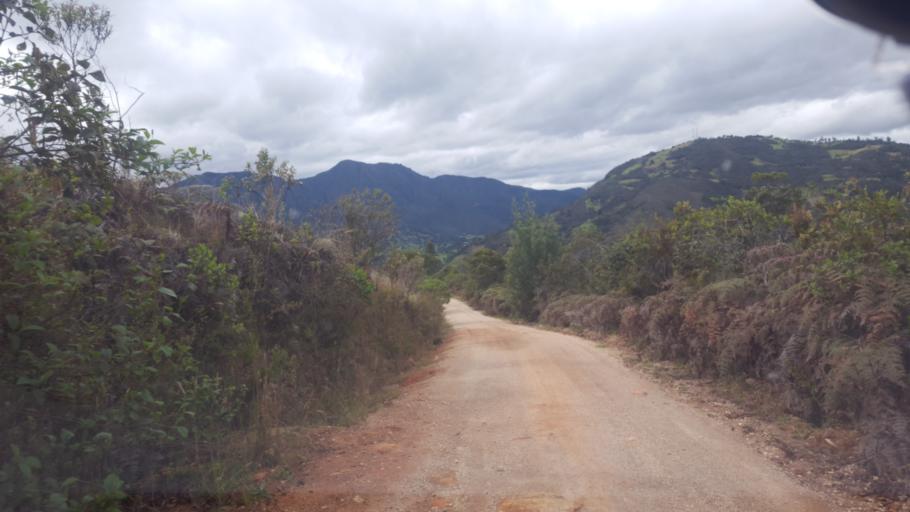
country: CO
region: Boyaca
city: Cerinza
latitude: 5.9929
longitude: -72.9508
